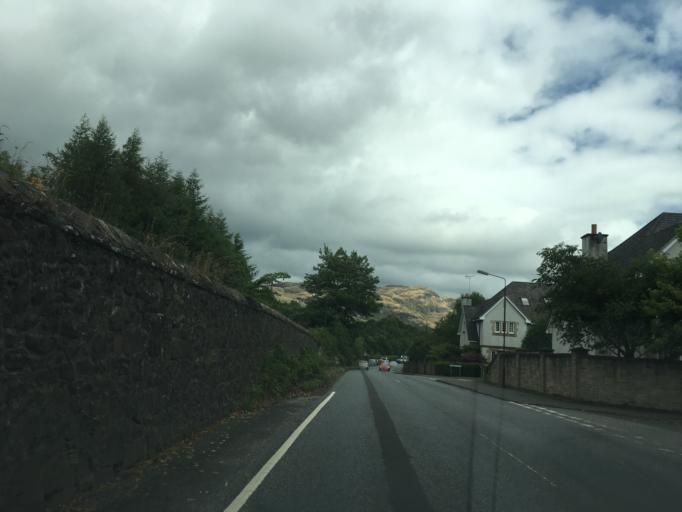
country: GB
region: Scotland
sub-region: Stirling
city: Stirling
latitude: 56.1401
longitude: -3.9209
